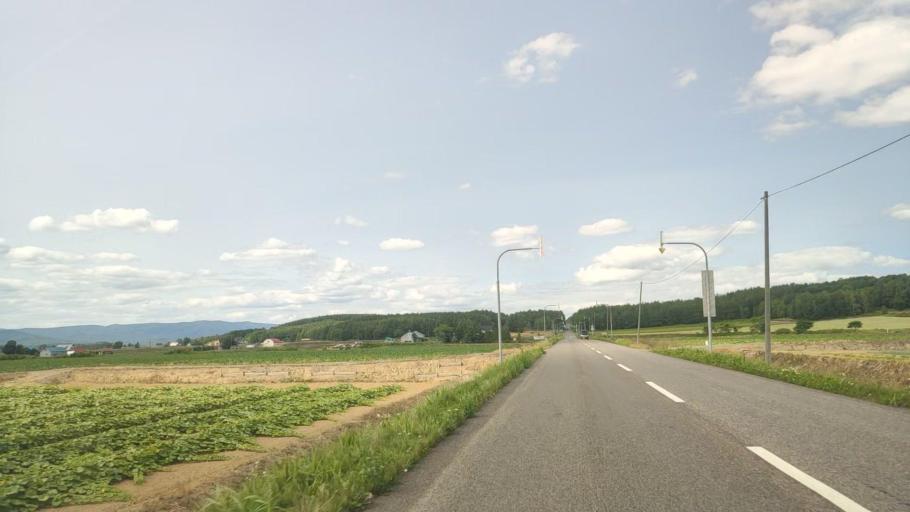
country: JP
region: Hokkaido
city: Nayoro
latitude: 44.2368
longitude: 142.4157
